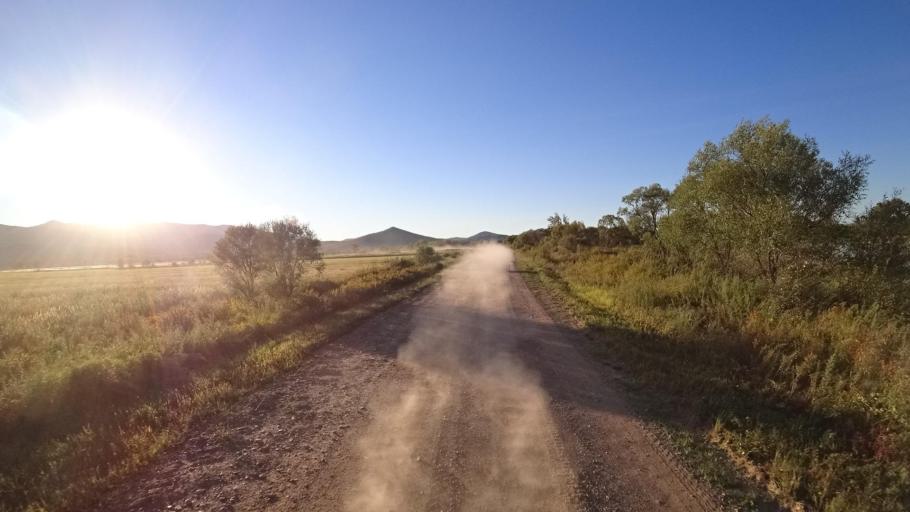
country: RU
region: Primorskiy
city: Kirovskiy
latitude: 44.8208
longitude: 133.6061
